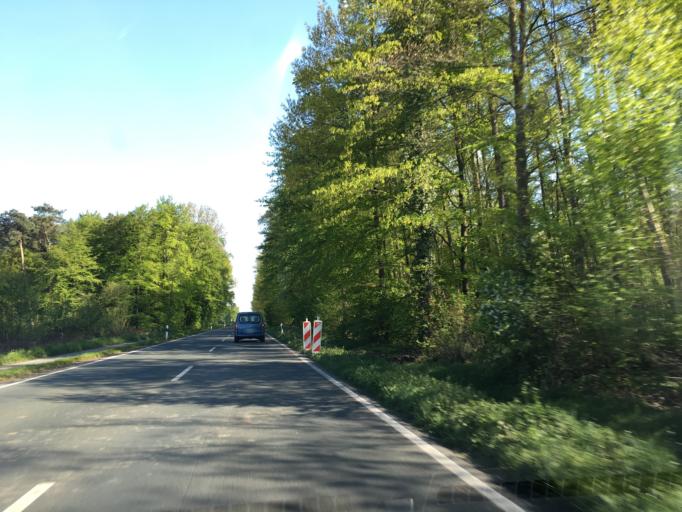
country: DE
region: North Rhine-Westphalia
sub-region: Regierungsbezirk Munster
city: Senden
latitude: 51.8464
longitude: 7.5096
